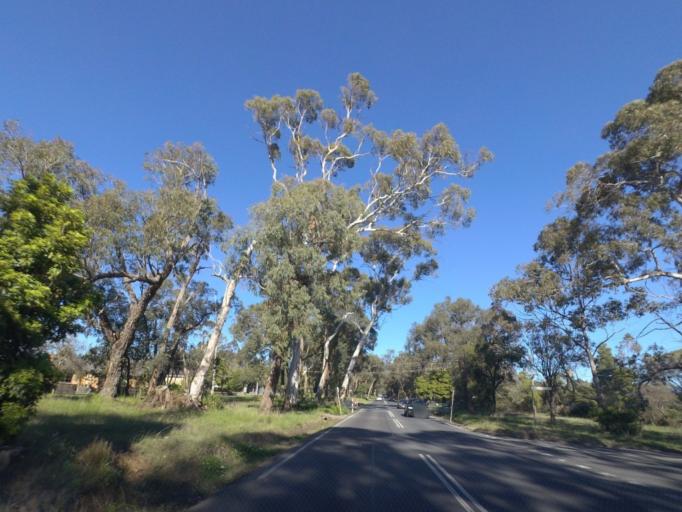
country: AU
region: Victoria
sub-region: Yarra Ranges
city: Kilsyth
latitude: -37.7955
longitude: 145.3237
